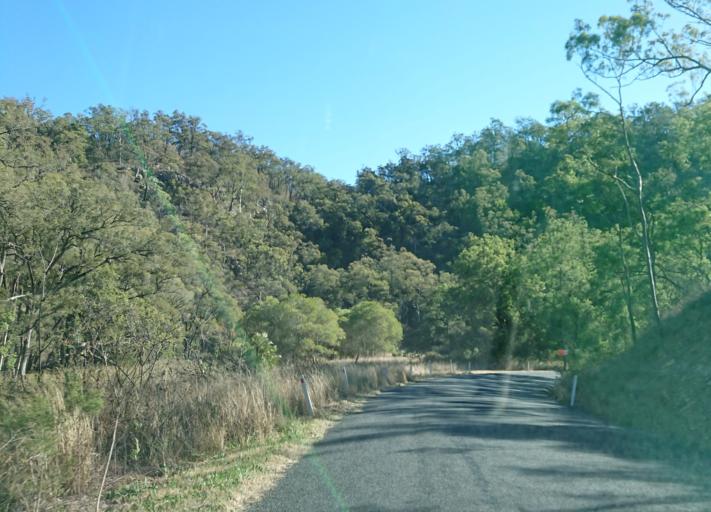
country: AU
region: Queensland
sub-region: Toowoomba
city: Top Camp
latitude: -27.7676
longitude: 152.0866
